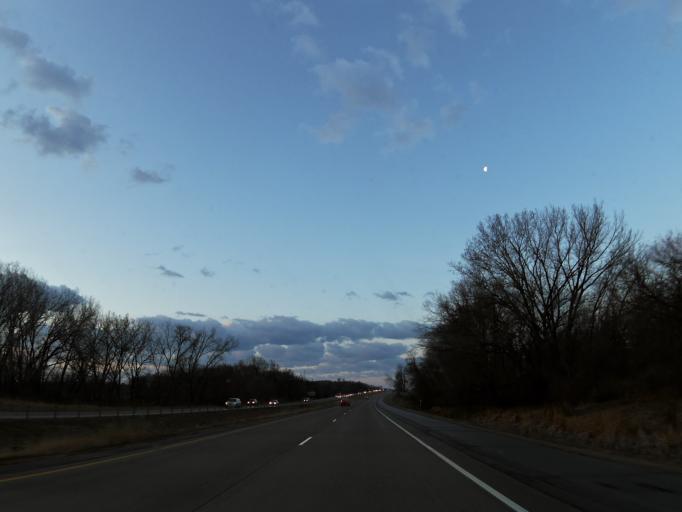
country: US
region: Minnesota
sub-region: Scott County
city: Elko New Market
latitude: 44.5893
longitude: -93.2981
